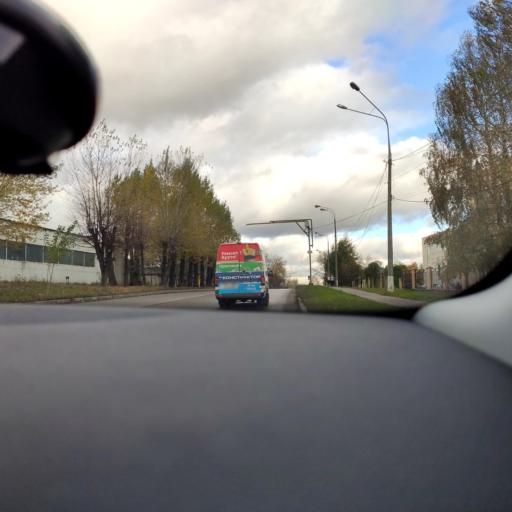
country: RU
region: Moskovskaya
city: Kotel'niki
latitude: 55.6400
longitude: 37.8391
